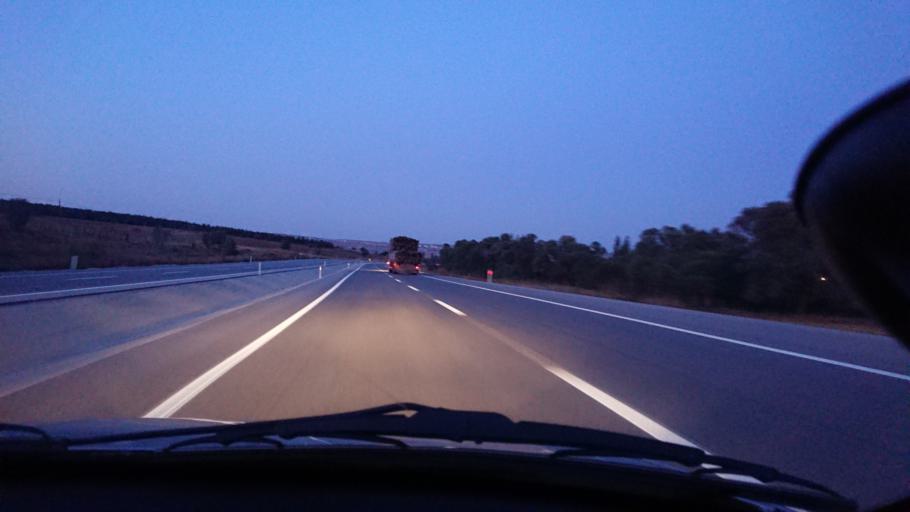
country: TR
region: Kuetahya
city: Cavdarhisar
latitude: 39.1200
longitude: 29.5316
